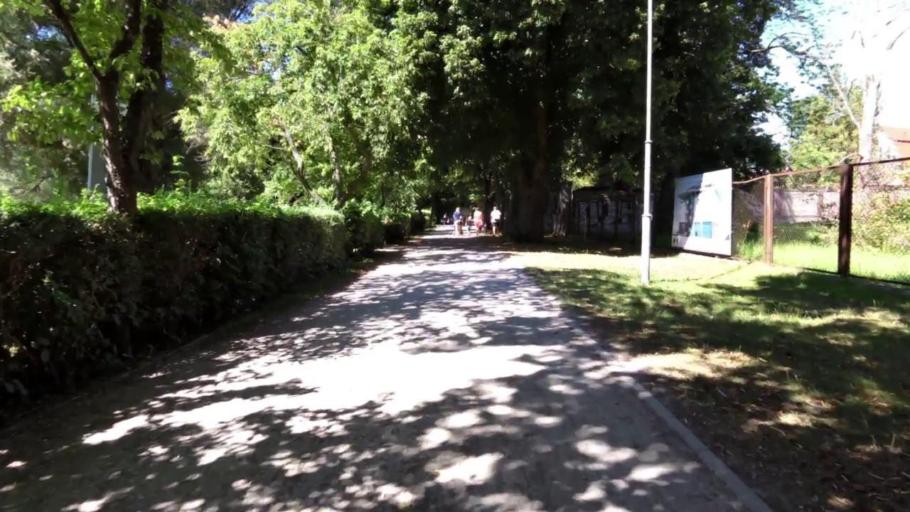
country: PL
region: West Pomeranian Voivodeship
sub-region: Powiat szczecinecki
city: Szczecinek
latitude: 53.7120
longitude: 16.6767
